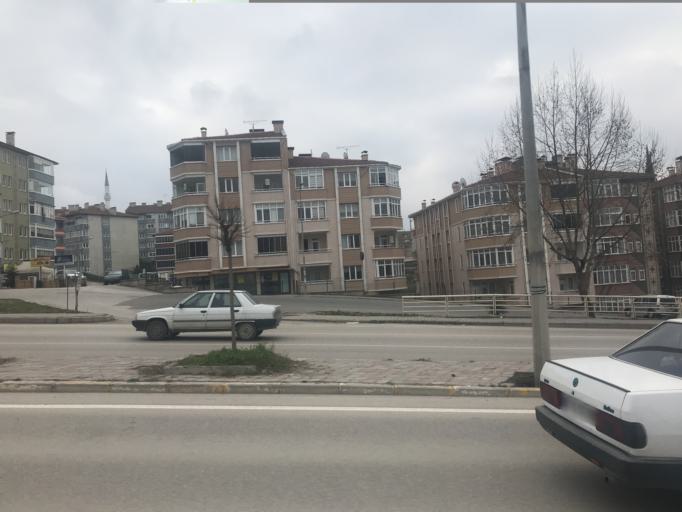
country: TR
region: Karabuk
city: Safranbolu
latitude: 41.2267
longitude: 32.6647
